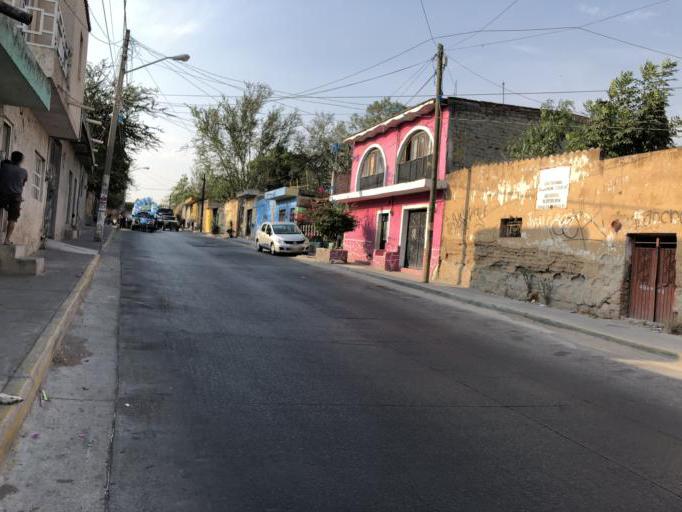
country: MX
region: Jalisco
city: Tlaquepaque
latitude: 20.6040
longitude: -103.2894
